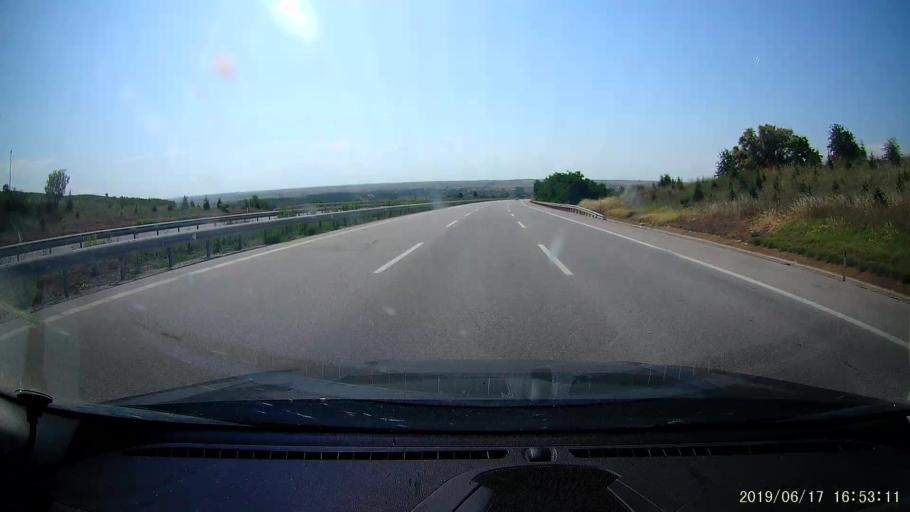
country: TR
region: Kirklareli
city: Inece
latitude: 41.5607
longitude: 27.0307
